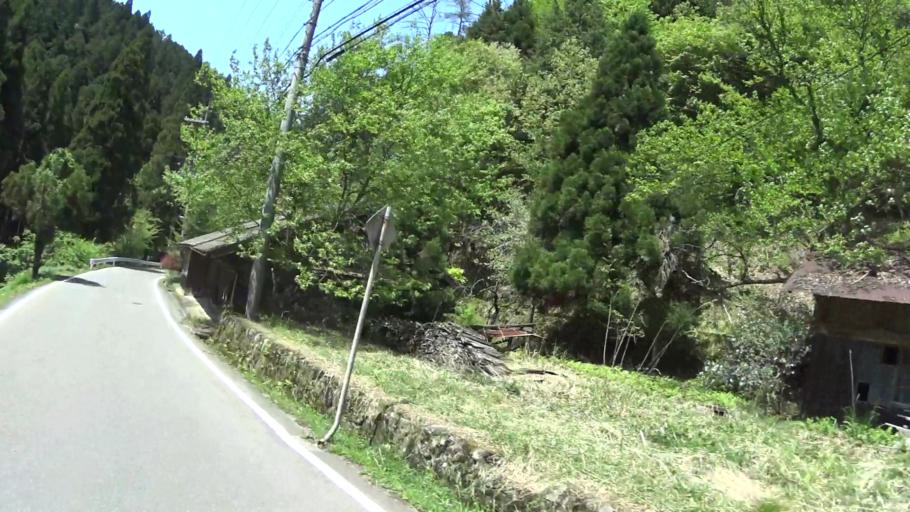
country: JP
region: Shiga Prefecture
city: Kitahama
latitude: 35.2074
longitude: 135.7791
